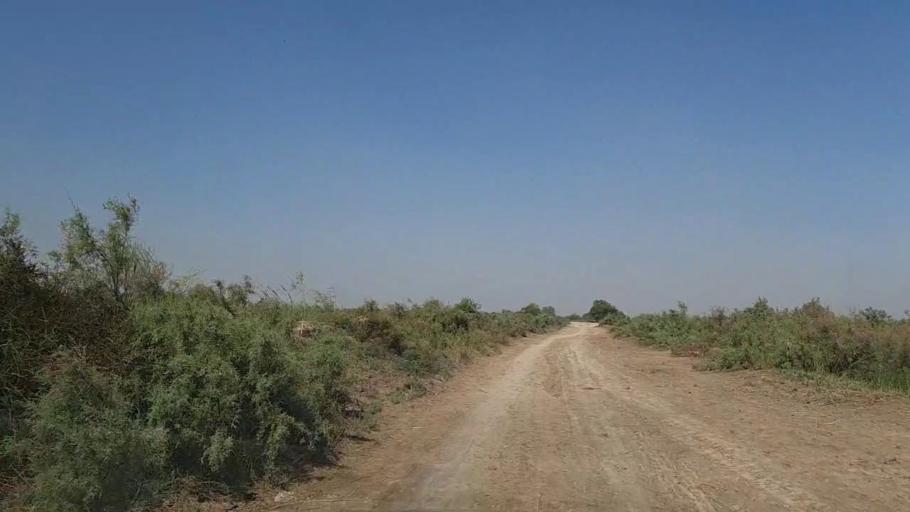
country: PK
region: Sindh
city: Daro Mehar
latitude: 24.8231
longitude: 68.1504
